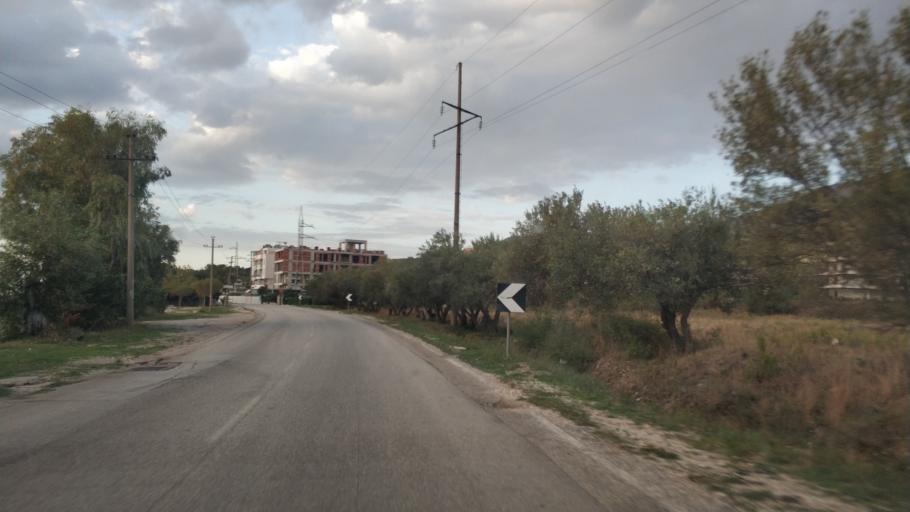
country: AL
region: Vlore
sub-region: Rrethi i Vlores
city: Orikum
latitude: 40.3513
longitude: 19.4856
